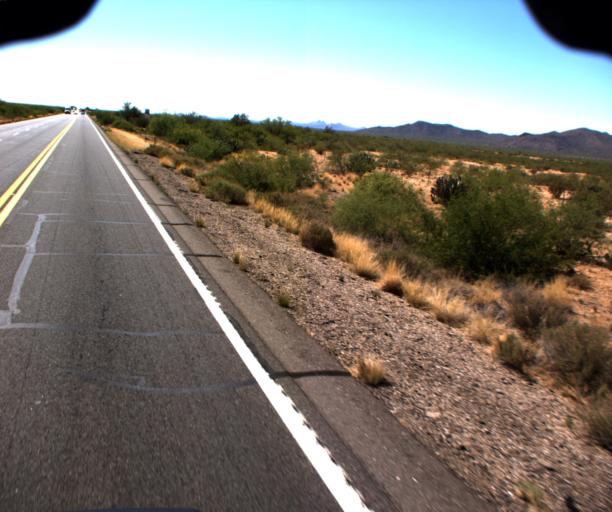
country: US
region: Arizona
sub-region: Yavapai County
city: Congress
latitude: 34.1307
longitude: -112.9611
